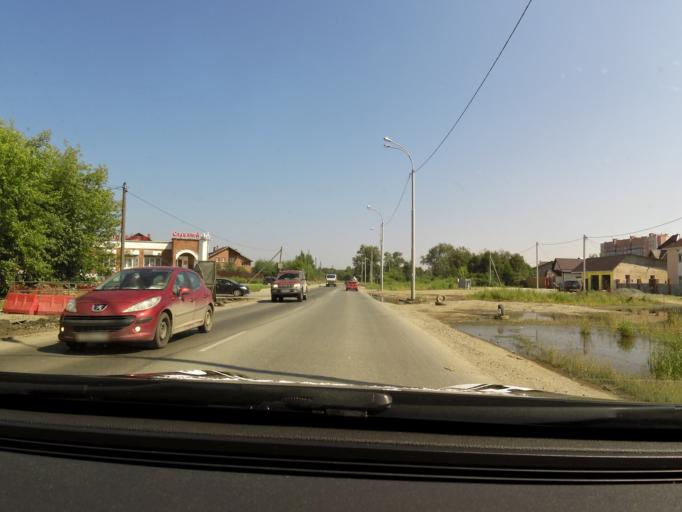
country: RU
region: Sverdlovsk
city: Shirokaya Rechka
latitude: 56.8068
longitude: 60.4962
